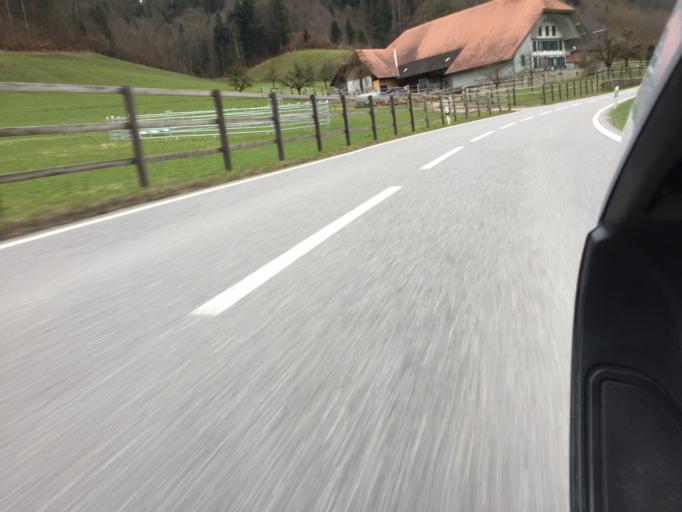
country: CH
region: Bern
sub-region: Emmental District
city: Krauchthal
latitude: 47.0234
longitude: 7.5781
